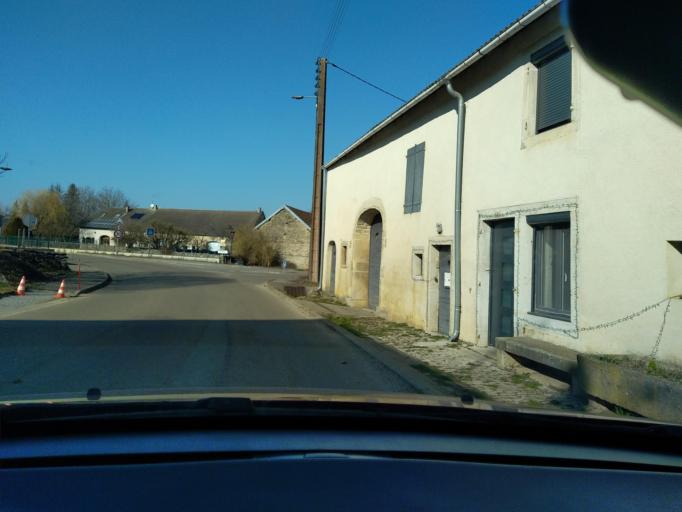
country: FR
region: Franche-Comte
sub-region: Departement du Jura
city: Perrigny
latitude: 46.6321
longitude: 5.6434
